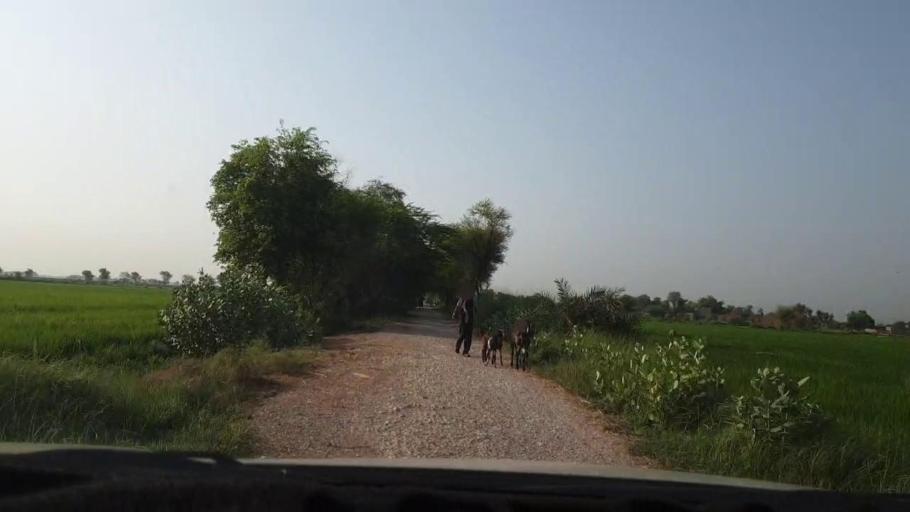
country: PK
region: Sindh
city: Larkana
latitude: 27.5056
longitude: 68.1741
